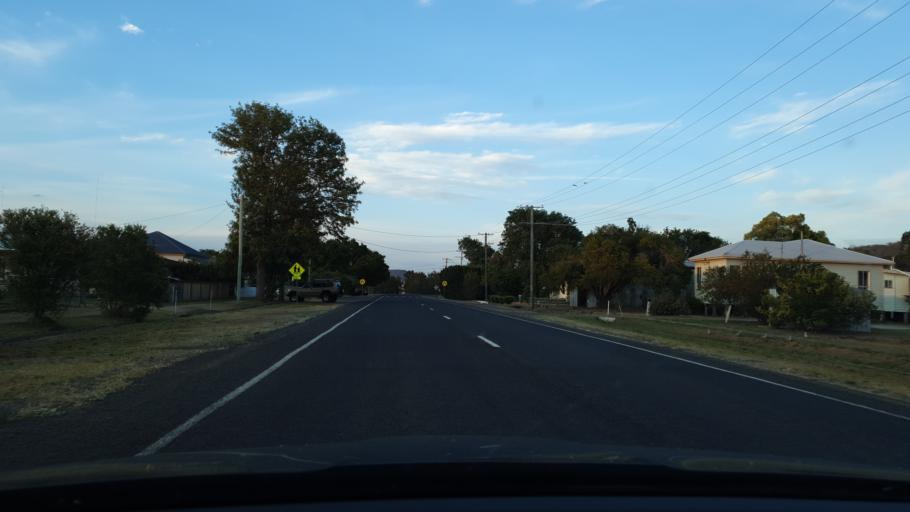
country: AU
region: Queensland
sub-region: Southern Downs
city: Warwick
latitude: -28.0331
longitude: 151.9808
